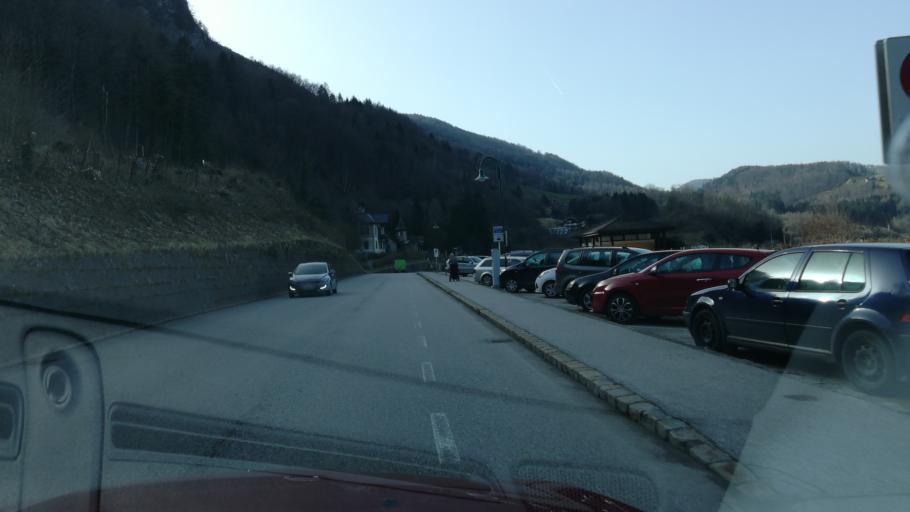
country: AT
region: Upper Austria
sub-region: Politischer Bezirk Gmunden
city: Ebensee
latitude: 47.8457
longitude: 13.7870
